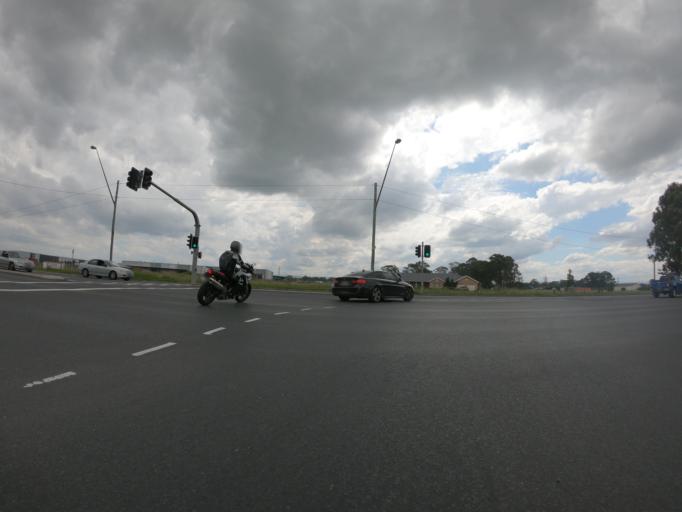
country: AU
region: New South Wales
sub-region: Blacktown
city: Mount Druitt
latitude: -33.8204
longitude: 150.7764
